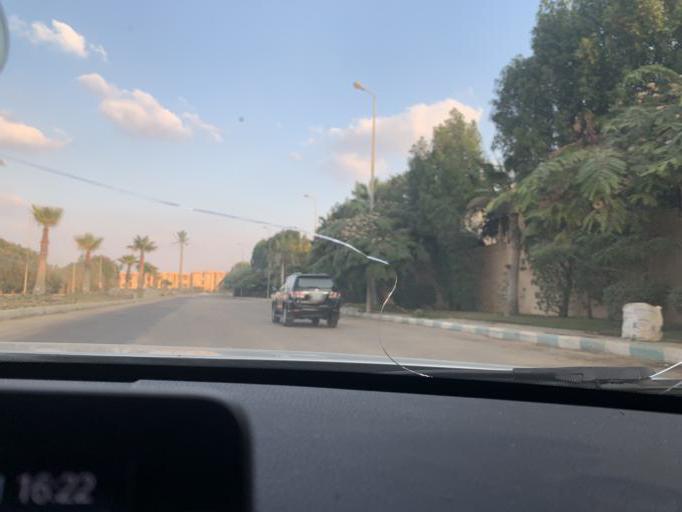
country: EG
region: Muhafazat al Qalyubiyah
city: Al Khankah
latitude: 30.0163
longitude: 31.4835
